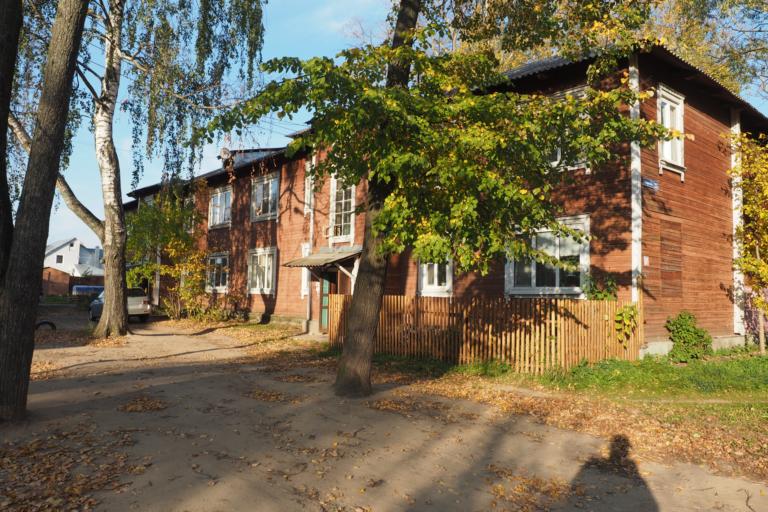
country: RU
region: Moskovskaya
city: Kurovskoye
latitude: 55.5761
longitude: 38.9066
